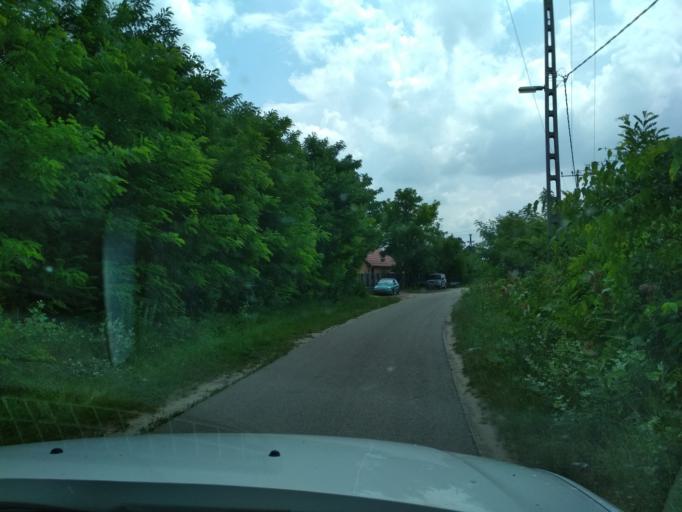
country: HU
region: Pest
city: Tapioszentmarton
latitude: 47.3735
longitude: 19.7561
